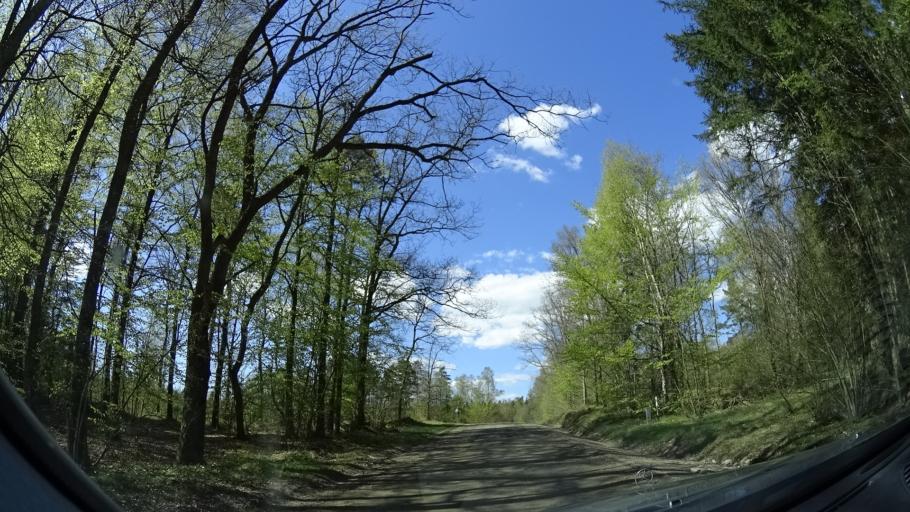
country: SE
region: Skane
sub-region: Hassleholms Kommun
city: Tormestorp
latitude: 56.0853
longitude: 13.6918
